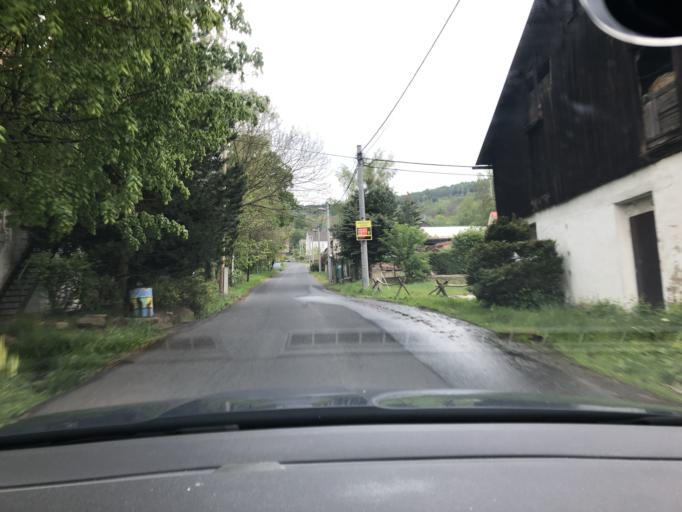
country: CZ
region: Ustecky
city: Libouchec
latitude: 50.7346
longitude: 14.0023
